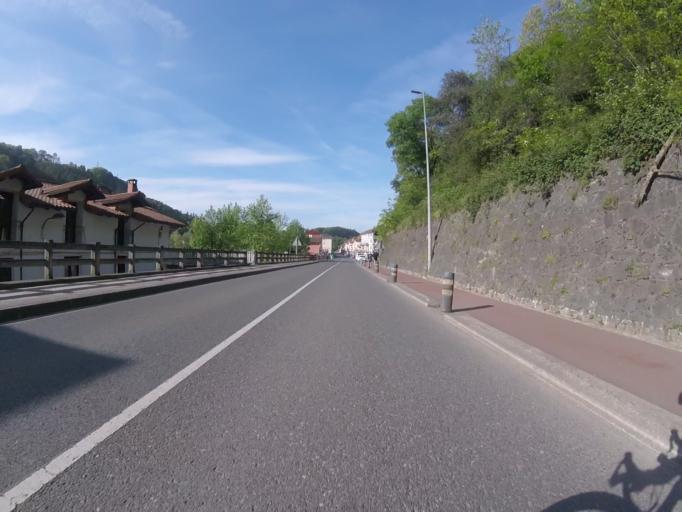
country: ES
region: Basque Country
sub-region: Provincia de Guipuzcoa
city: Isasondo
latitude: 43.0702
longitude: -2.1629
